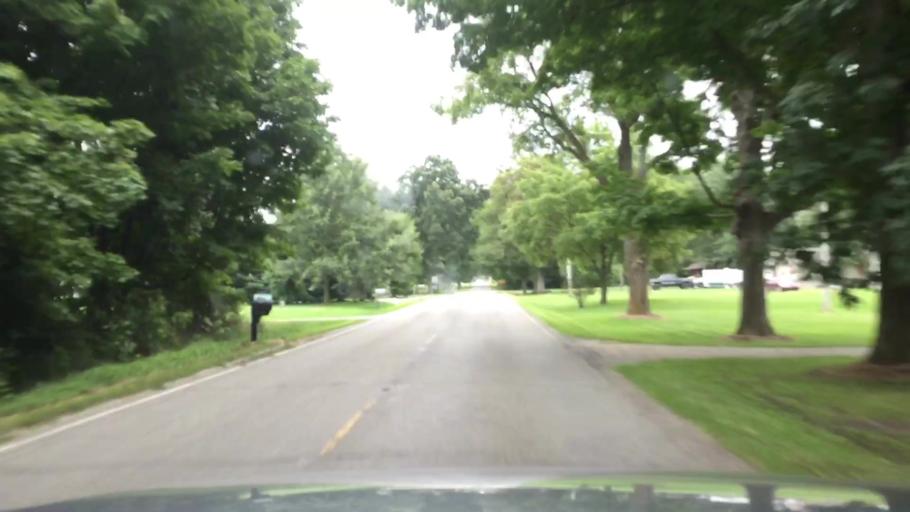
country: US
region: Michigan
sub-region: Shiawassee County
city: Durand
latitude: 42.8237
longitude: -83.9617
